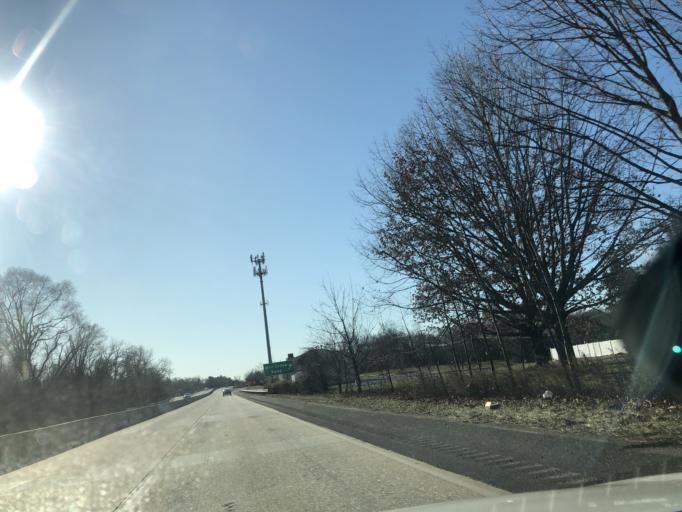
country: US
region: Pennsylvania
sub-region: Bucks County
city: Levittown
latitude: 40.1620
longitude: -74.8117
